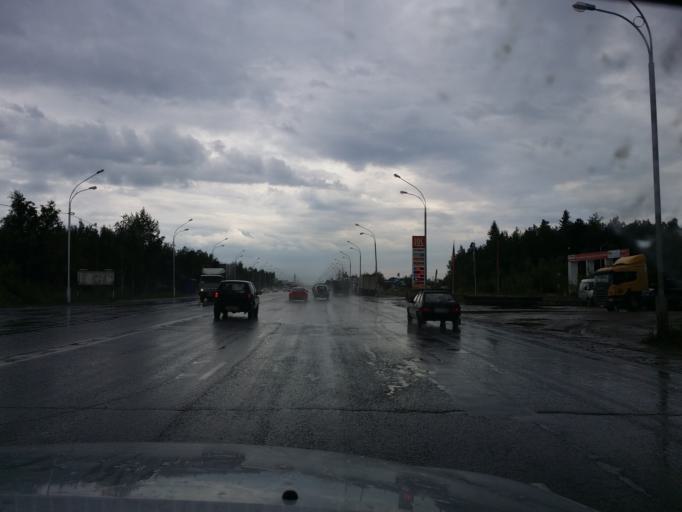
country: RU
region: Khanty-Mansiyskiy Avtonomnyy Okrug
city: Nizhnevartovsk
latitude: 60.9671
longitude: 76.5307
